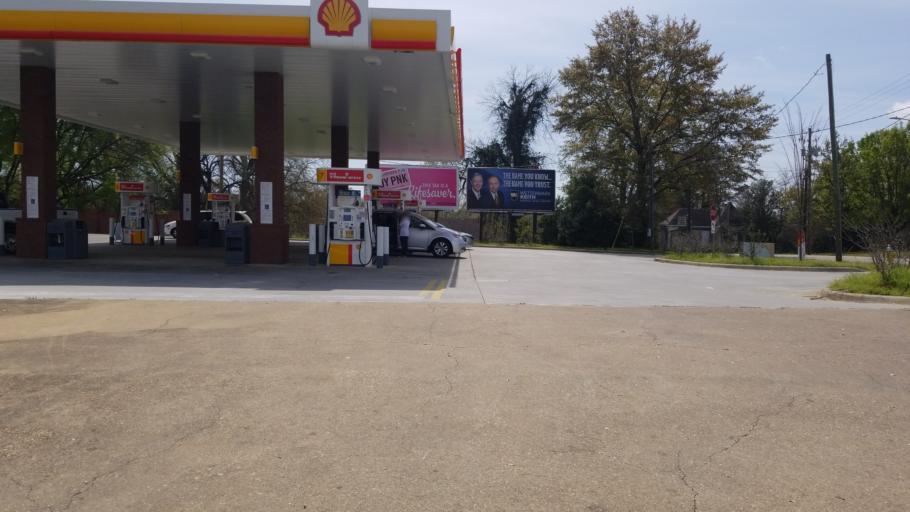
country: US
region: Alabama
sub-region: Montgomery County
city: Montgomery
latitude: 32.3672
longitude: -86.3086
